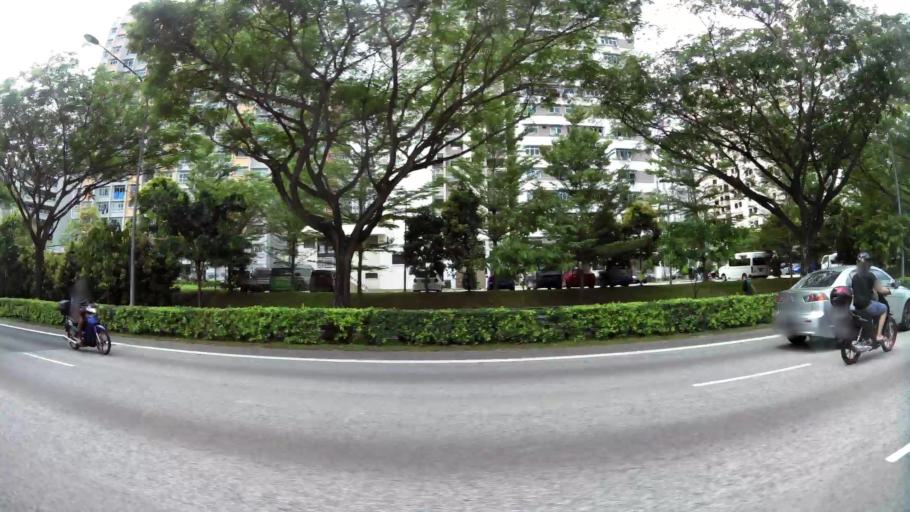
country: MY
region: Johor
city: Kampung Pasir Gudang Baru
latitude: 1.3912
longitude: 103.9096
